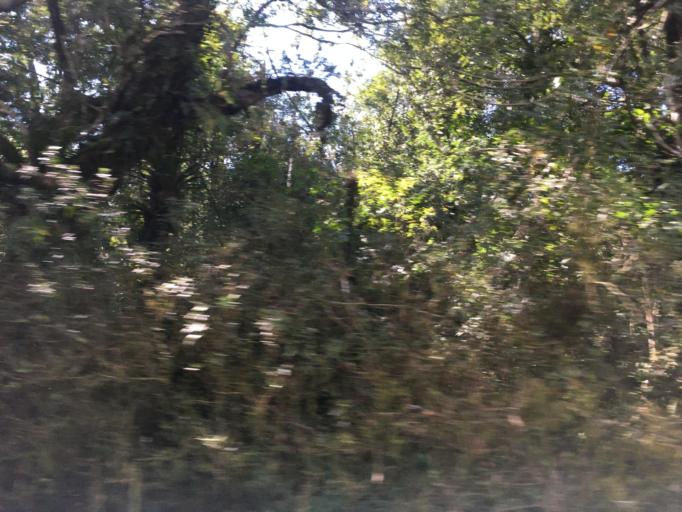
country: TW
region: Taiwan
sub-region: Yilan
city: Yilan
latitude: 24.7566
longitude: 121.5934
